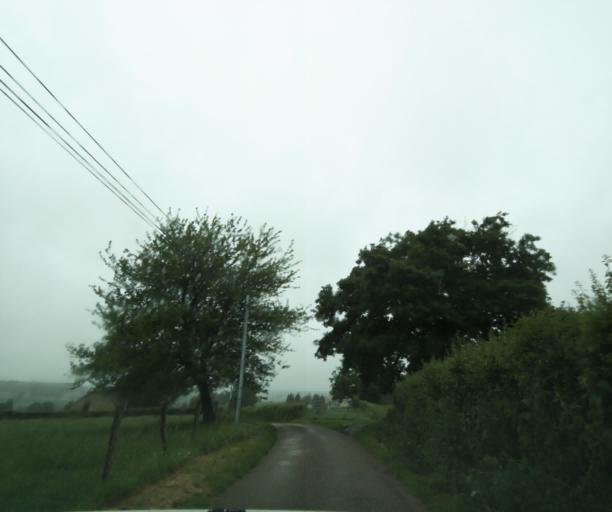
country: FR
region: Bourgogne
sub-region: Departement de Saone-et-Loire
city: Charolles
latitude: 46.4112
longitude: 4.2665
